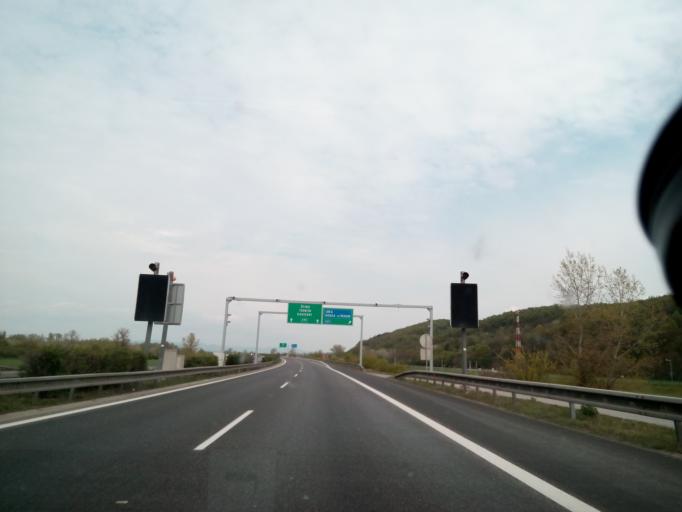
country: SK
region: Trnavsky
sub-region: Okres Trnava
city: Piestany
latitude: 48.6678
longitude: 17.8722
